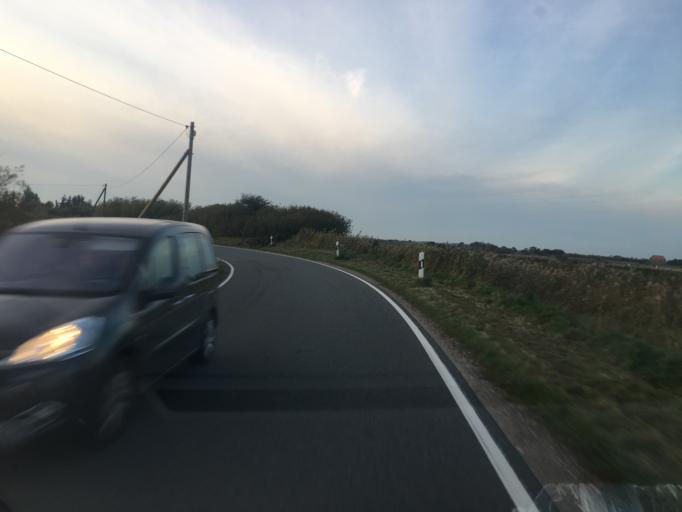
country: DE
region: Schleswig-Holstein
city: Aventoft
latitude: 54.9047
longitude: 8.8378
